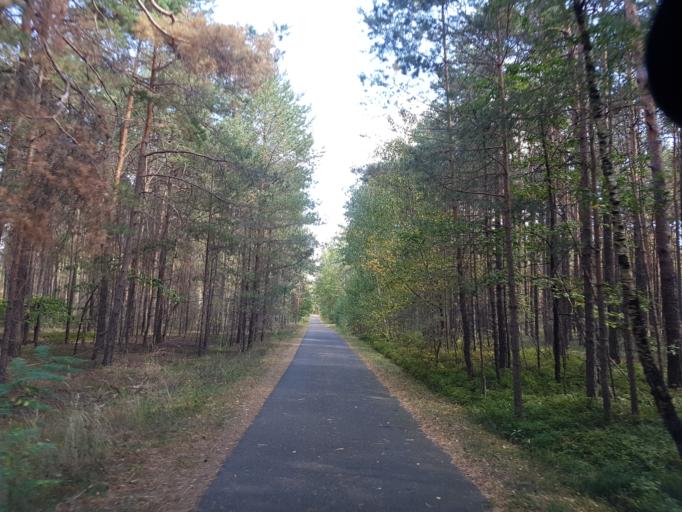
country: DE
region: Brandenburg
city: Finsterwalde
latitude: 51.5996
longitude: 13.7623
